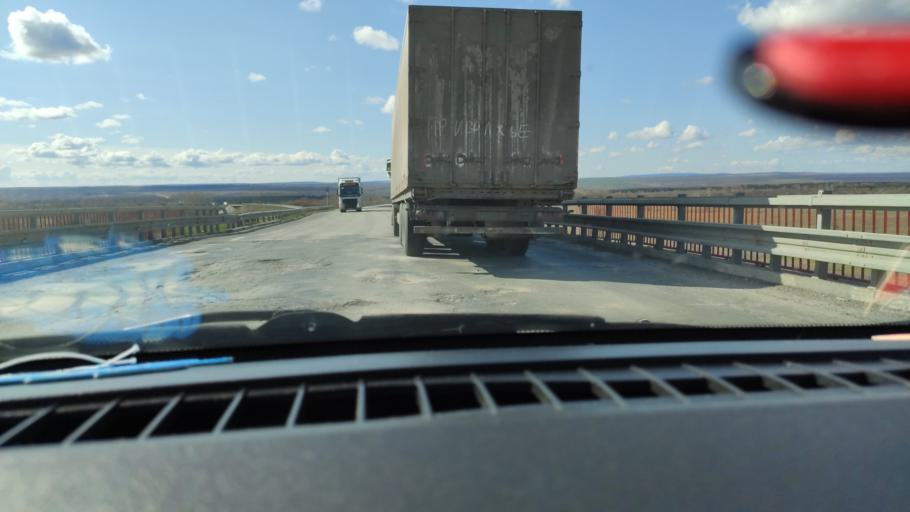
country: RU
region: Samara
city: Varlamovo
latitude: 53.1717
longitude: 48.2810
